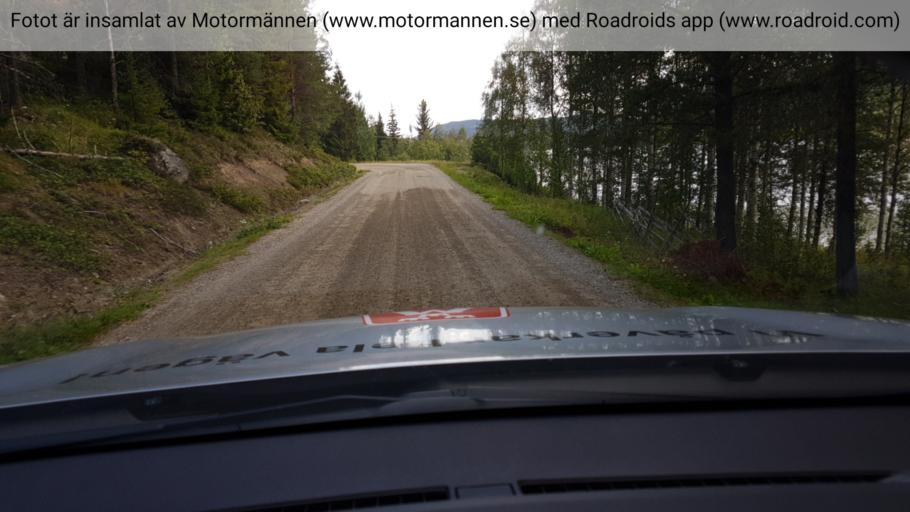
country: SE
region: Jaemtland
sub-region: Ragunda Kommun
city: Hammarstrand
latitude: 63.3450
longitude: 15.9817
